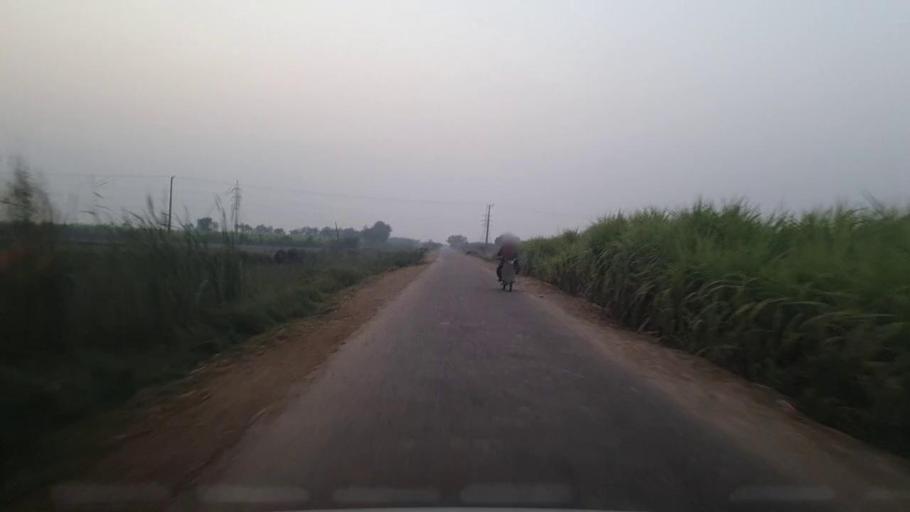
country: PK
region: Sindh
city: Kot Diji
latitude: 27.3408
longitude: 68.6145
